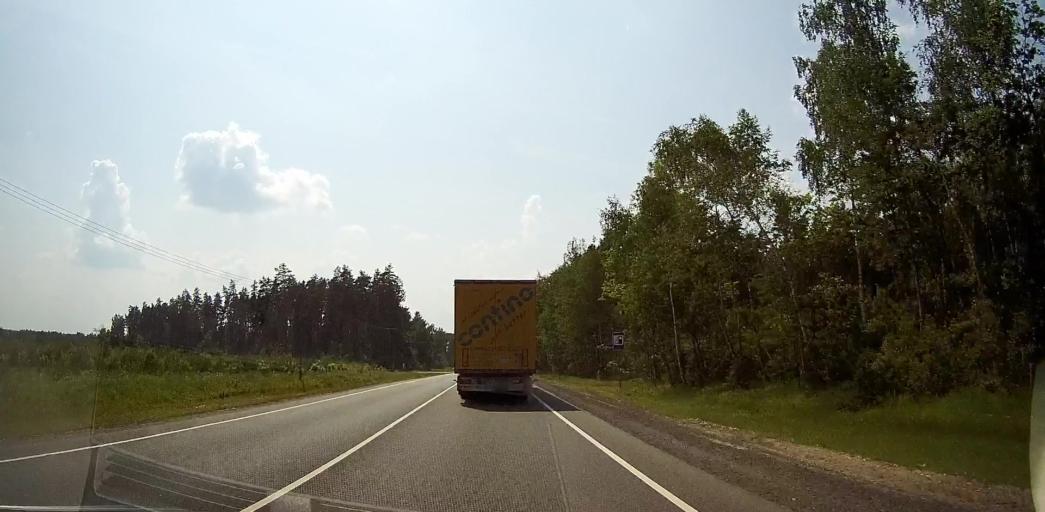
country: RU
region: Moskovskaya
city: Meshcherino
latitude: 55.2051
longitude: 38.3791
